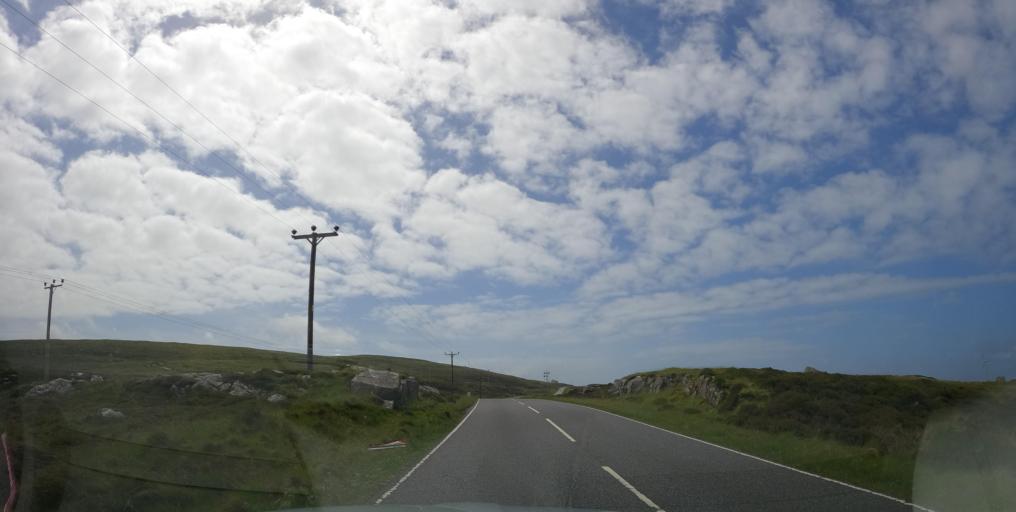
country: GB
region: Scotland
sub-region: Eilean Siar
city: Isle of South Uist
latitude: 57.2387
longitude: -7.3879
